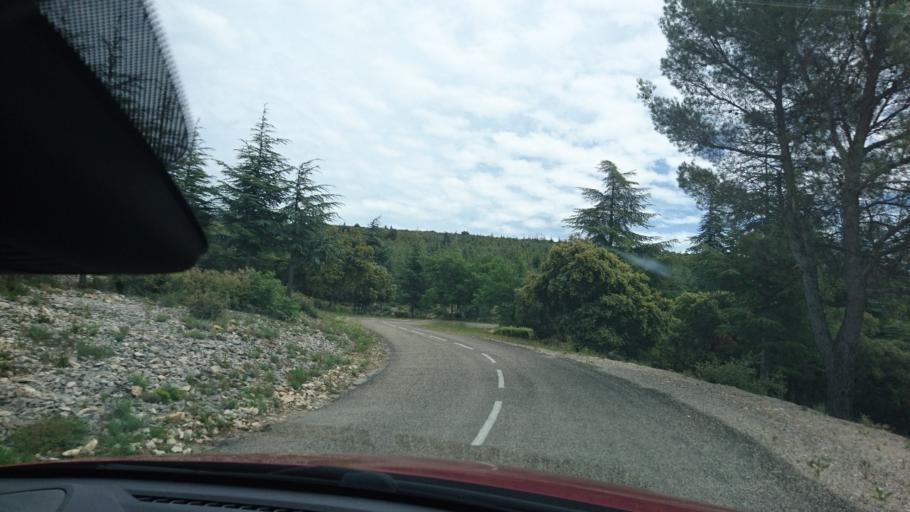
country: FR
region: Provence-Alpes-Cote d'Azur
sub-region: Departement du Vaucluse
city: Villes-sur-Auzon
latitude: 44.0995
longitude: 5.2507
